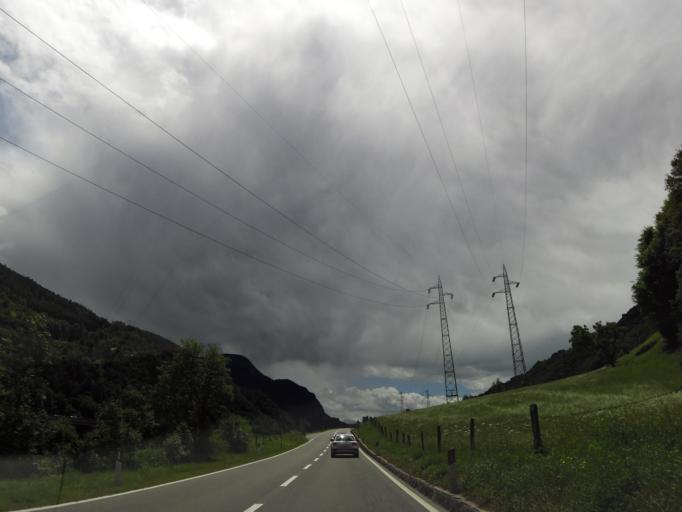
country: IT
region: Trentino-Alto Adige
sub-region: Bolzano
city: Villandro - Villanders
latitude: 46.6170
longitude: 11.5378
